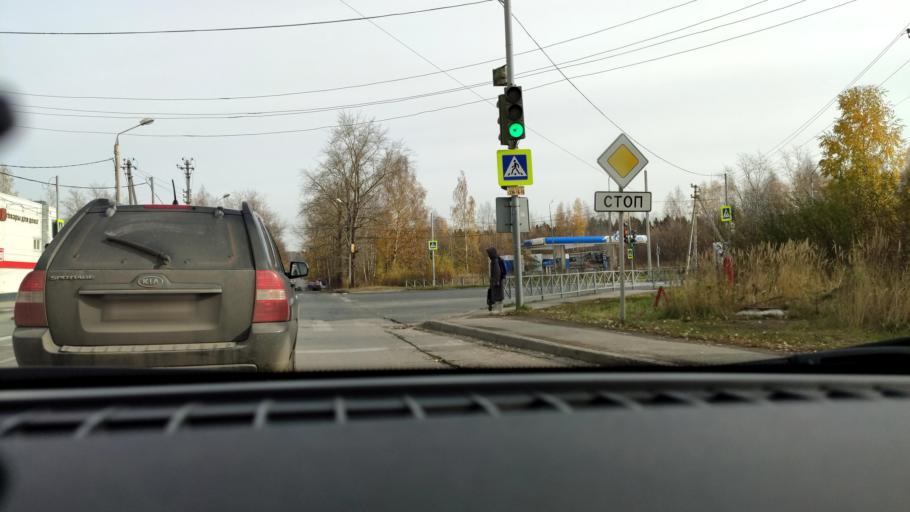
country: RU
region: Perm
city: Polazna
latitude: 58.1330
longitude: 56.4025
